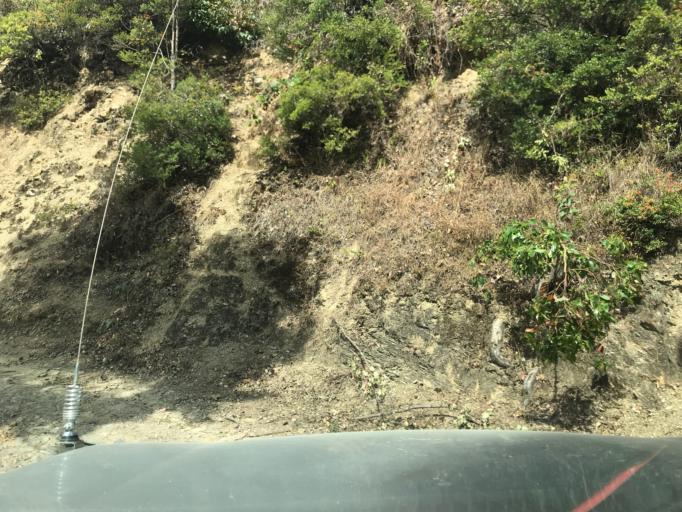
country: TL
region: Ainaro
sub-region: Ainaro
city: Ainaro
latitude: -8.8838
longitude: 125.5260
